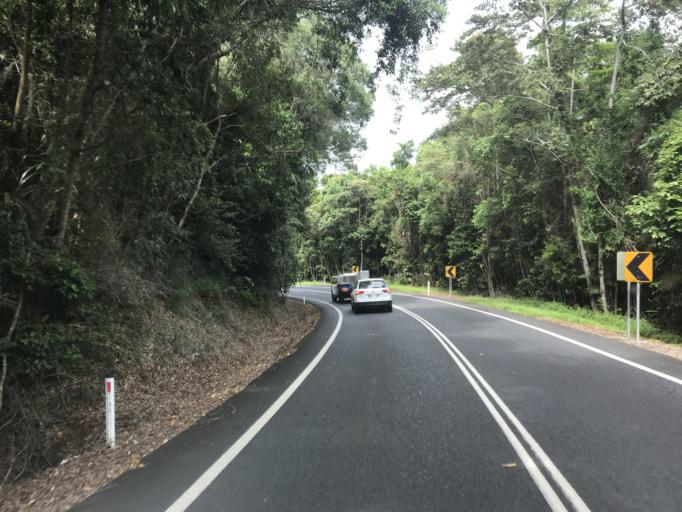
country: AU
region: Queensland
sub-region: Cassowary Coast
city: Innisfail
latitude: -17.8669
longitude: 146.0727
